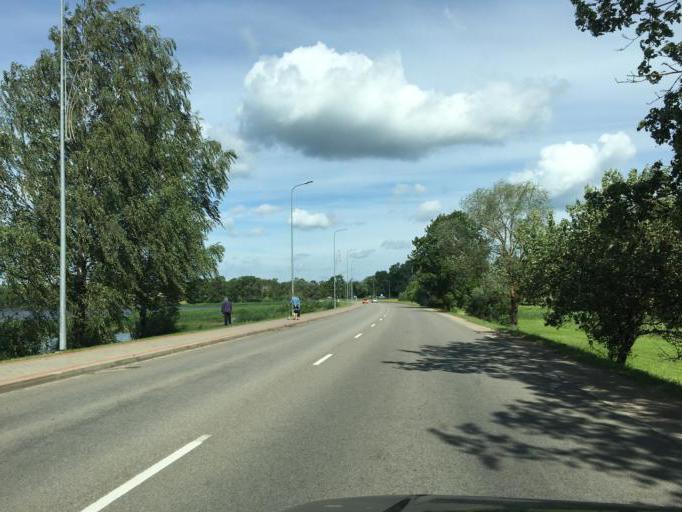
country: LV
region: Balvu Rajons
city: Balvi
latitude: 57.1355
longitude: 27.2602
